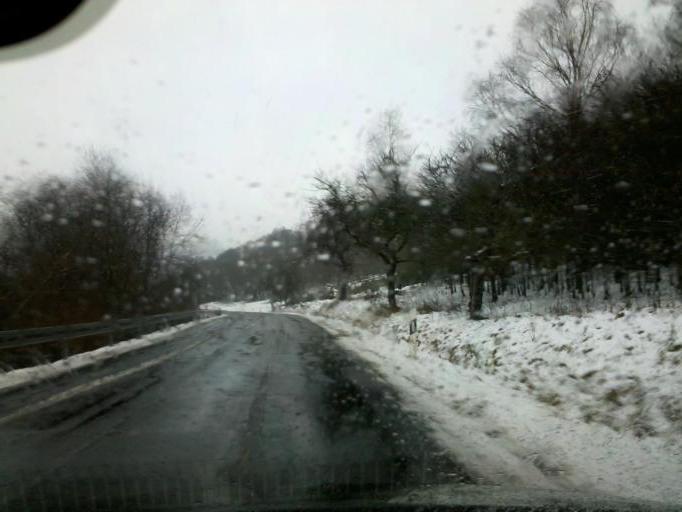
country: DE
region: Hesse
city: Dillenburg
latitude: 50.8109
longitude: 8.2825
